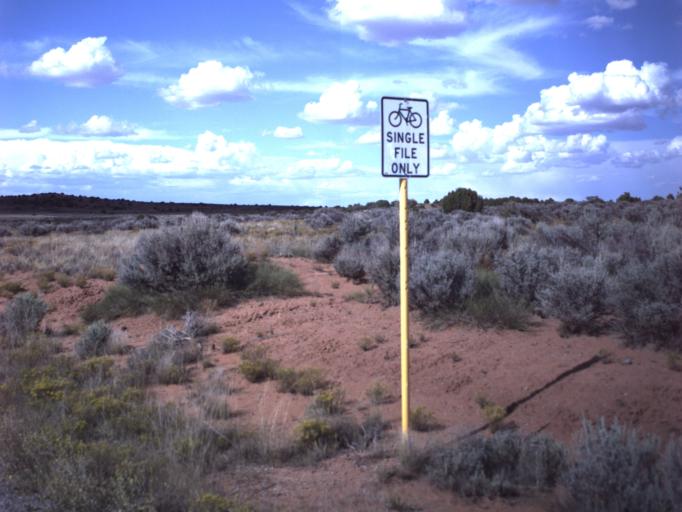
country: US
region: Utah
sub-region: Grand County
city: Moab
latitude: 38.5176
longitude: -109.7304
